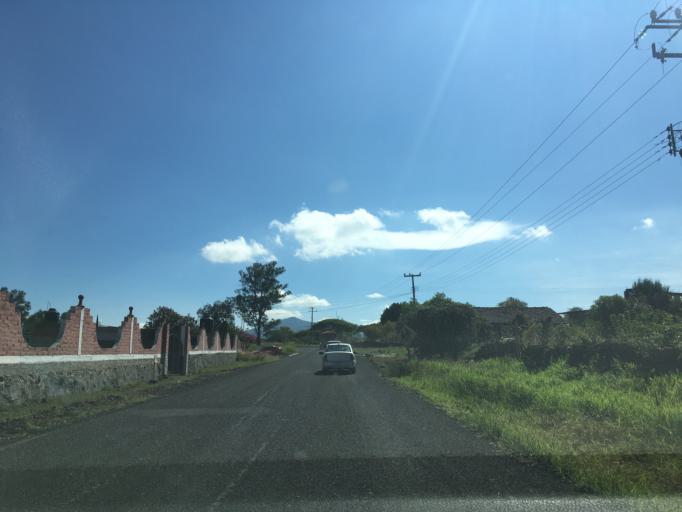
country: MX
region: Mexico
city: Tlazazalca
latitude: 19.9721
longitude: -102.0934
